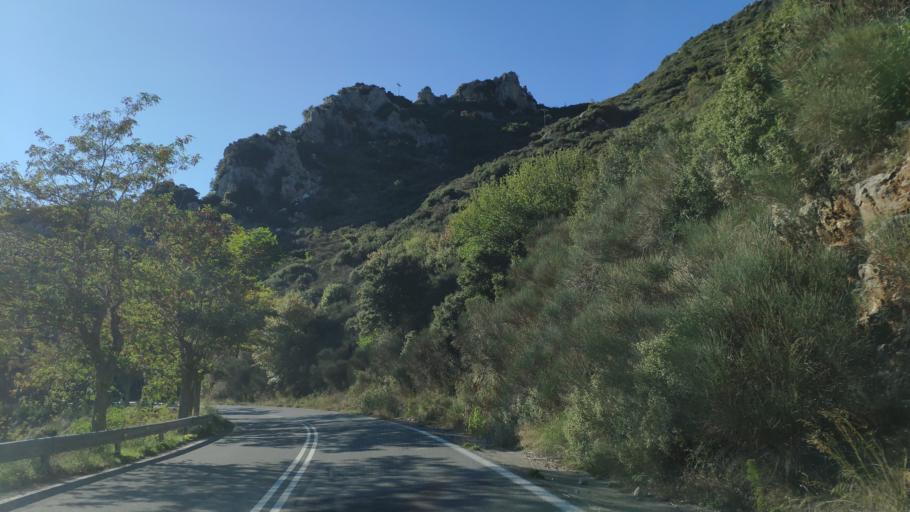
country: GR
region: Peloponnese
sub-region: Nomos Arkadias
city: Dimitsana
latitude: 37.5517
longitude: 22.0729
